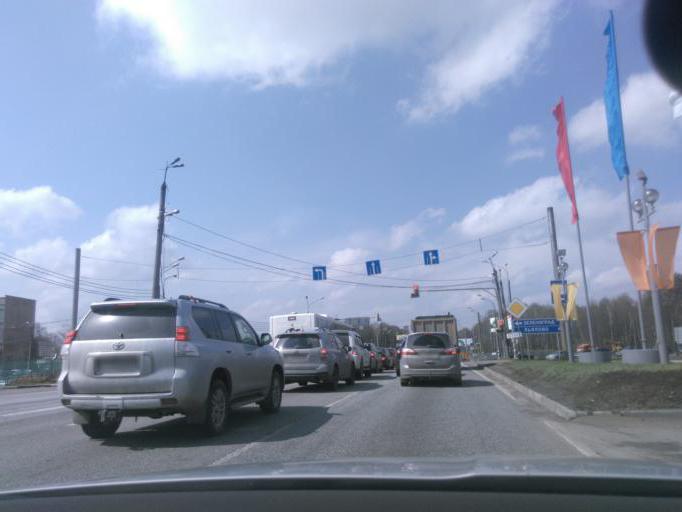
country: RU
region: Moskovskaya
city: Mendeleyevo
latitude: 56.0143
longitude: 37.2079
